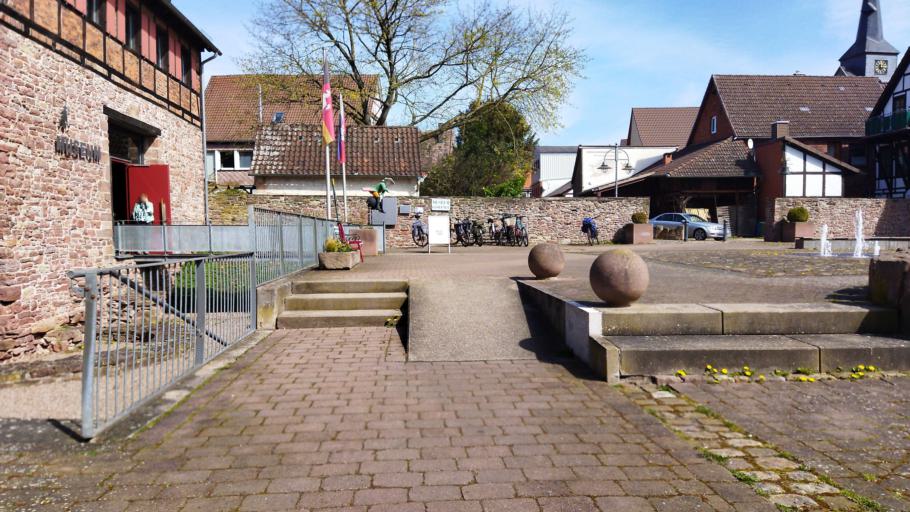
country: DE
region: Lower Saxony
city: Bodenwerder
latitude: 51.9763
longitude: 9.5141
